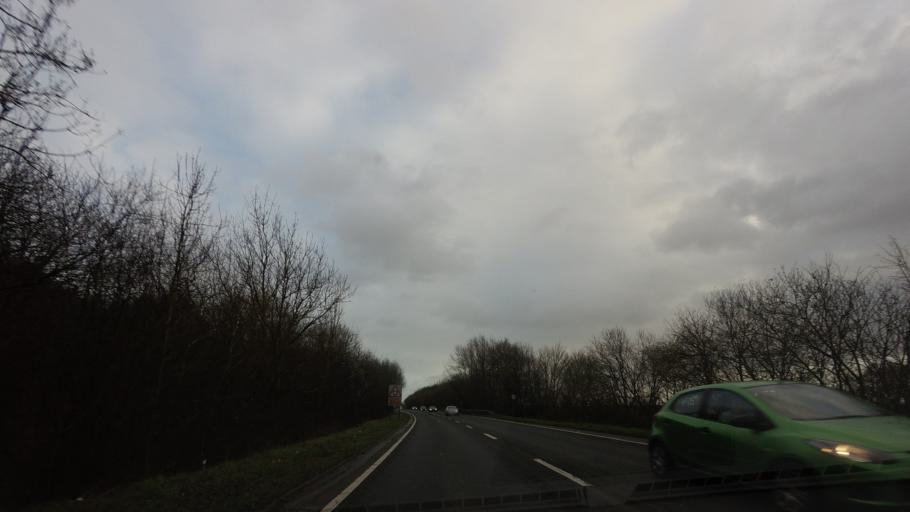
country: GB
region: England
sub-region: Kent
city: East Peckham
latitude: 51.2263
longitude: 0.3915
